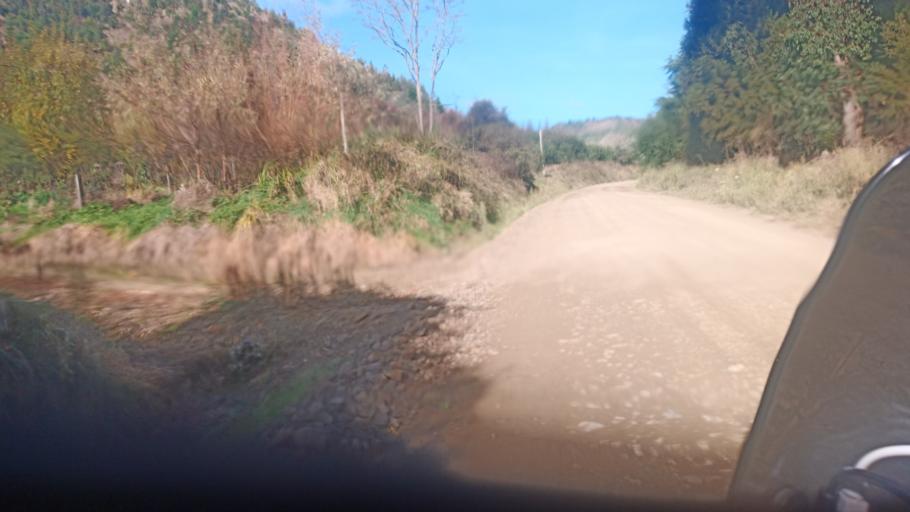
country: NZ
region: Bay of Plenty
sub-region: Opotiki District
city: Opotiki
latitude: -38.4189
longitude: 177.5581
